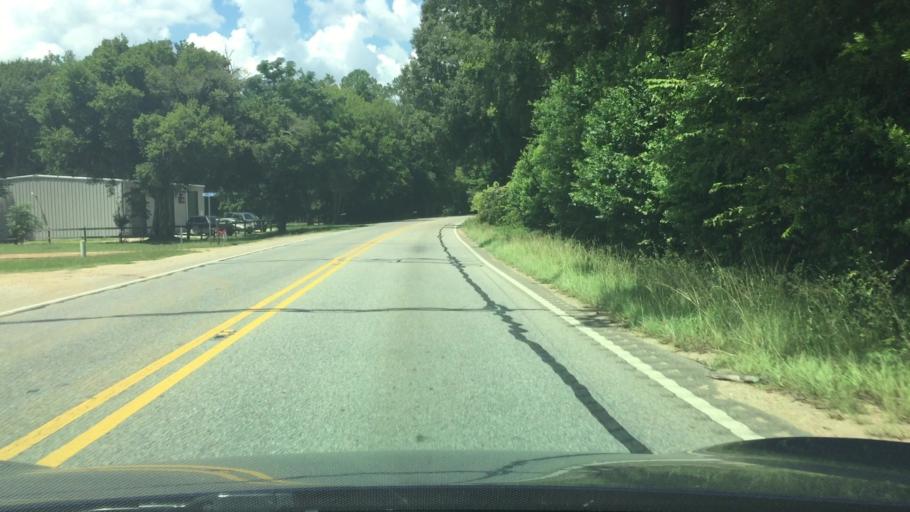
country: US
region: Alabama
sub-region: Montgomery County
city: Pike Road
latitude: 32.3658
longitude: -86.0424
